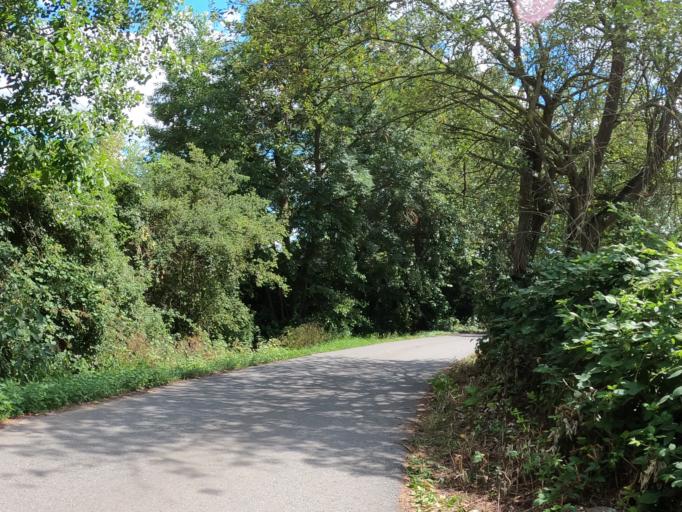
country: DE
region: Hesse
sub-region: Regierungsbezirk Darmstadt
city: Nauheim
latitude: 49.9508
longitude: 8.4718
